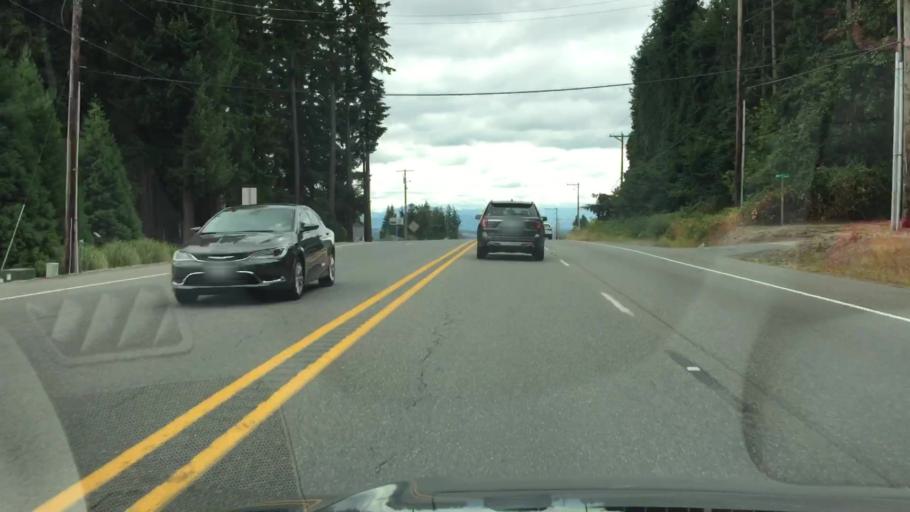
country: US
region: Washington
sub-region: Pierce County
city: Graham
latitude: 47.0288
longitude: -122.2961
